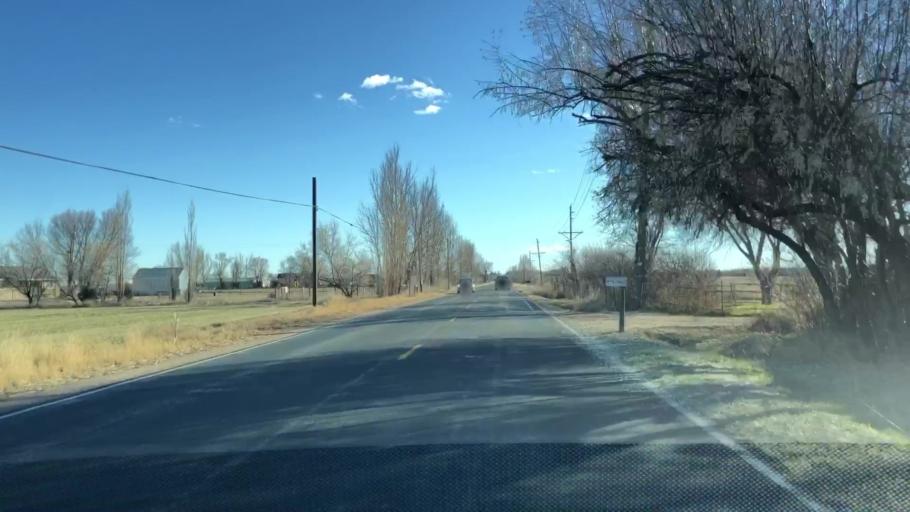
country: US
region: Colorado
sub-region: Larimer County
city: Fort Collins
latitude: 40.5492
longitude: -104.9824
